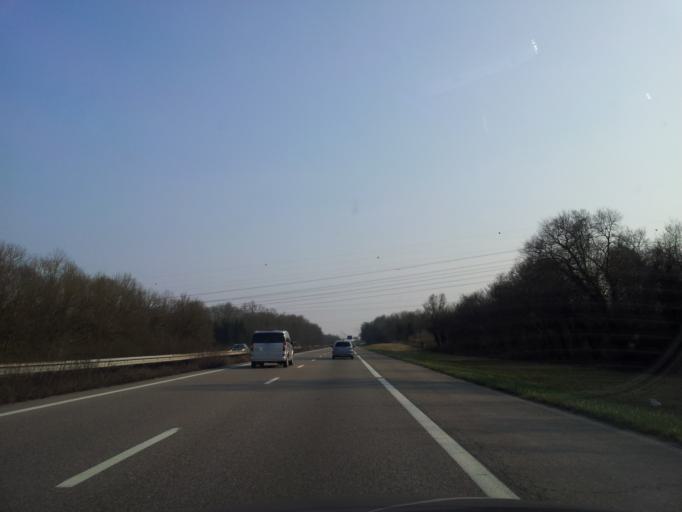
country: FR
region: Alsace
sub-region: Departement du Haut-Rhin
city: Bartenheim
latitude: 47.6467
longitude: 7.4941
